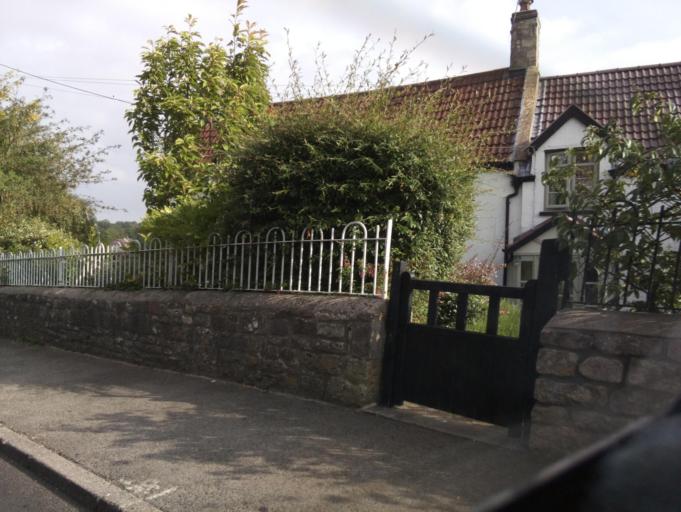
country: GB
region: England
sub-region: North Somerset
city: Winford
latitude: 51.3816
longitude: -2.6608
